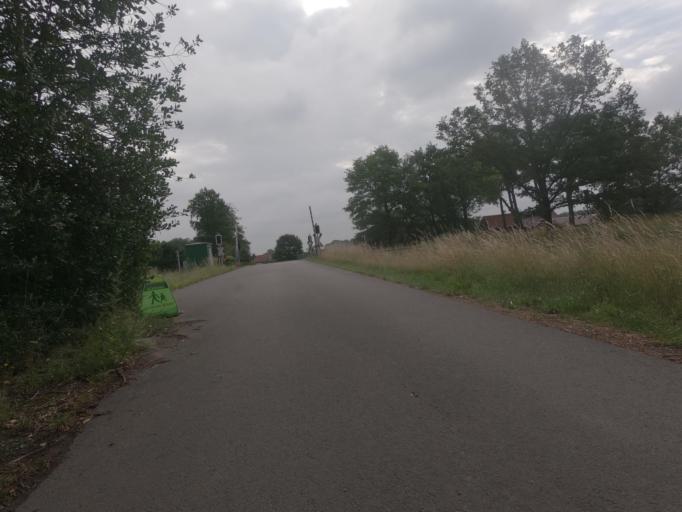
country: DE
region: Lower Saxony
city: Quendorf
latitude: 52.3400
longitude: 7.1713
